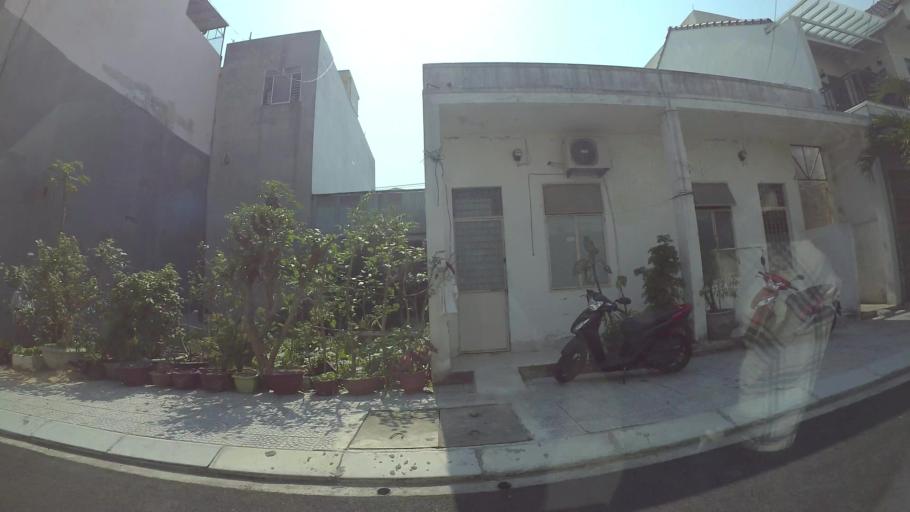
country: VN
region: Da Nang
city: Ngu Hanh Son
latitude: 16.0239
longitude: 108.2508
